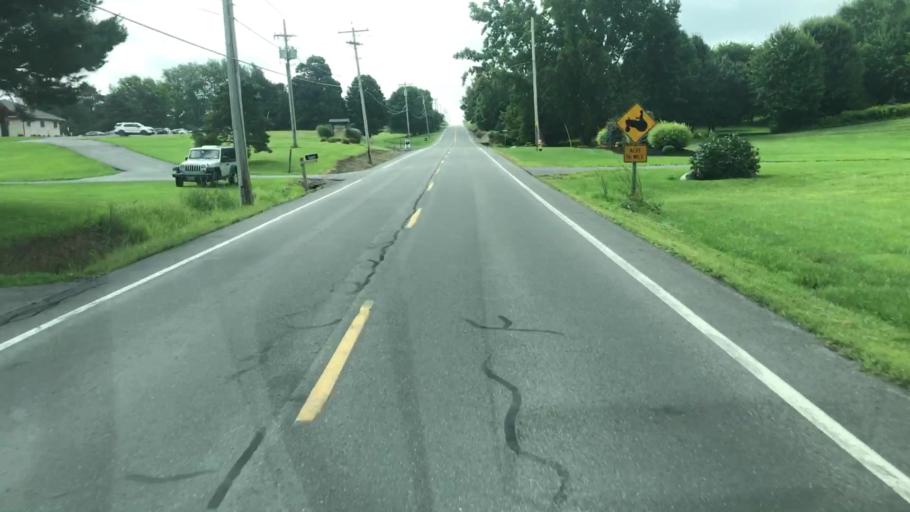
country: US
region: New York
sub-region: Onondaga County
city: Peru
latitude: 43.0476
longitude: -76.3661
